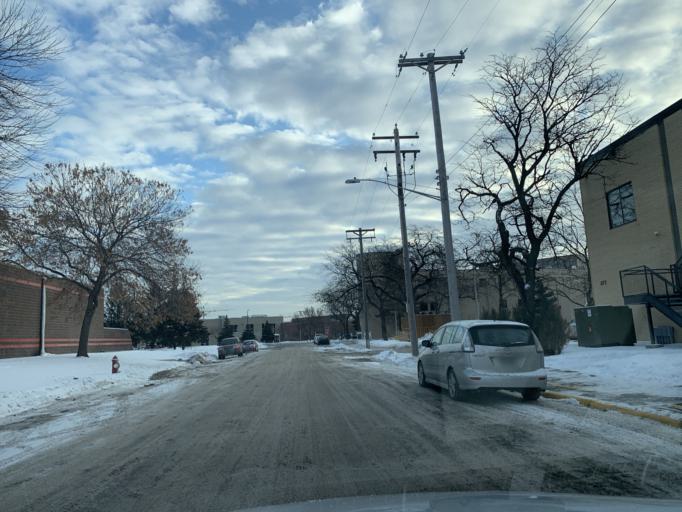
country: US
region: Minnesota
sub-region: Hennepin County
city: Minneapolis
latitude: 44.9909
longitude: -93.2826
